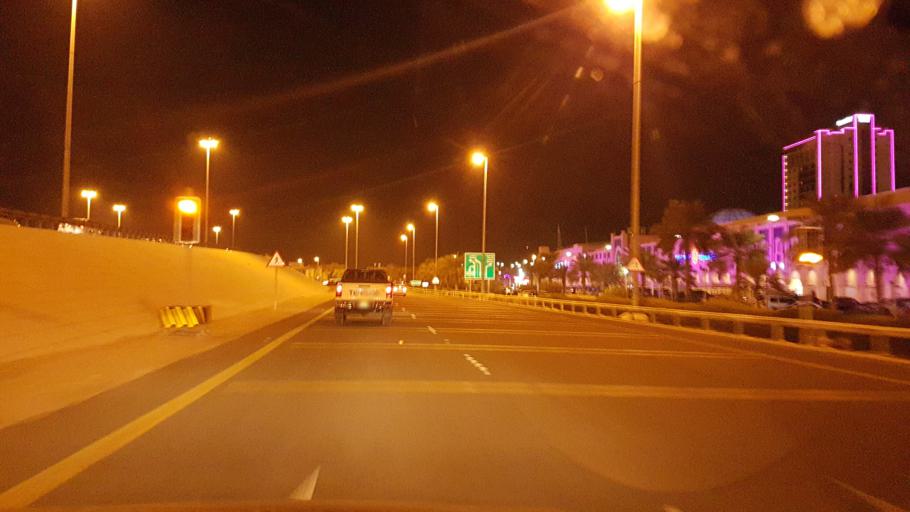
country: BH
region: Manama
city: Jidd Hafs
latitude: 26.2314
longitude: 50.5380
